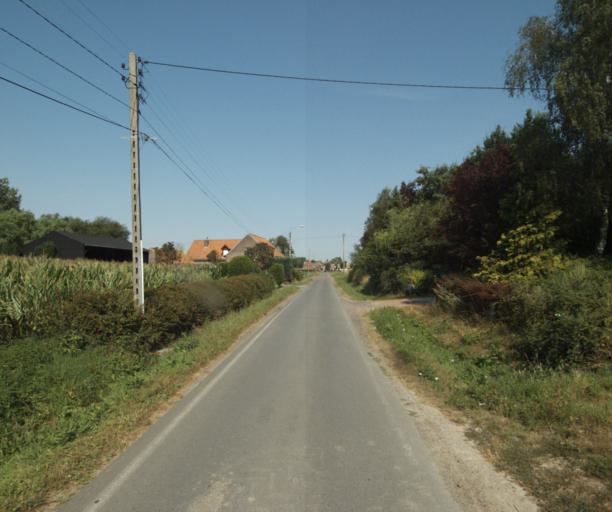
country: FR
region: Nord-Pas-de-Calais
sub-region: Departement du Nord
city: Comines
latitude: 50.7533
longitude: 3.0178
